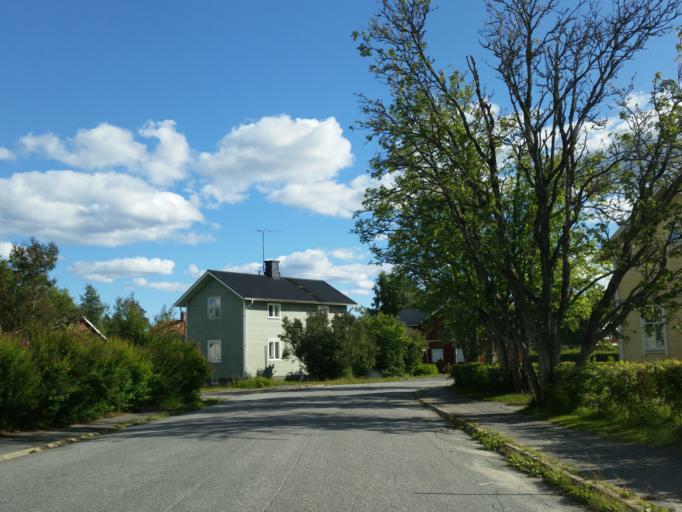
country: SE
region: Vaesterbotten
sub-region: Robertsfors Kommun
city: Robertsfors
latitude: 64.1914
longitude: 20.8592
